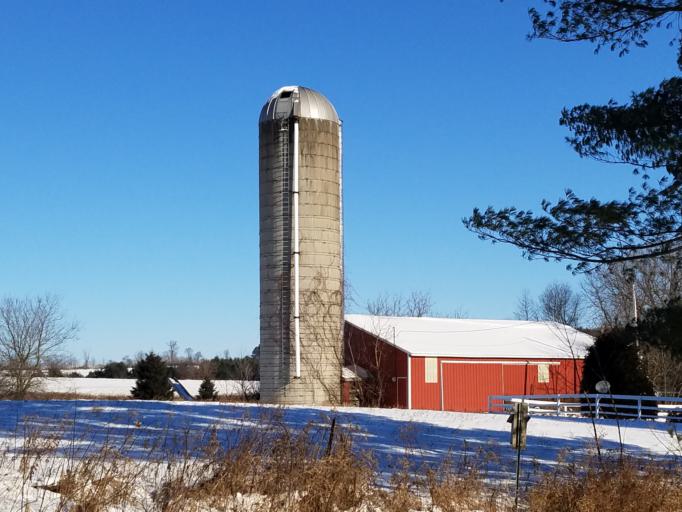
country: US
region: Wisconsin
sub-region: Clark County
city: Loyal
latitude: 44.5963
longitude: -90.4539
